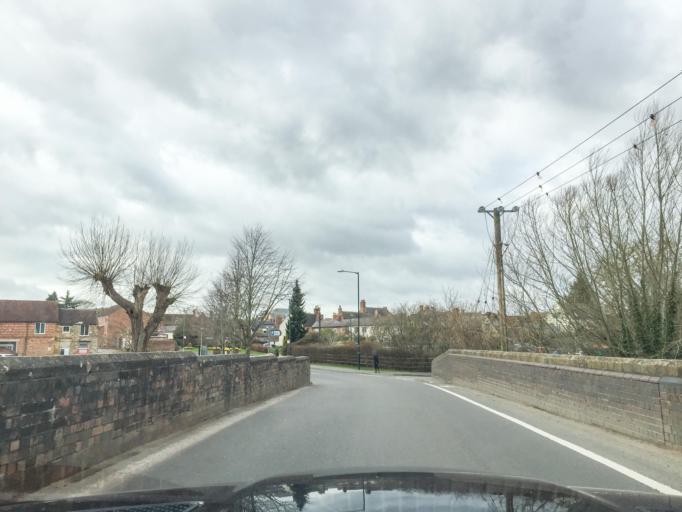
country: GB
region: England
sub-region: Warwickshire
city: Shipston on Stour
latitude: 52.0618
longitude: -1.6216
